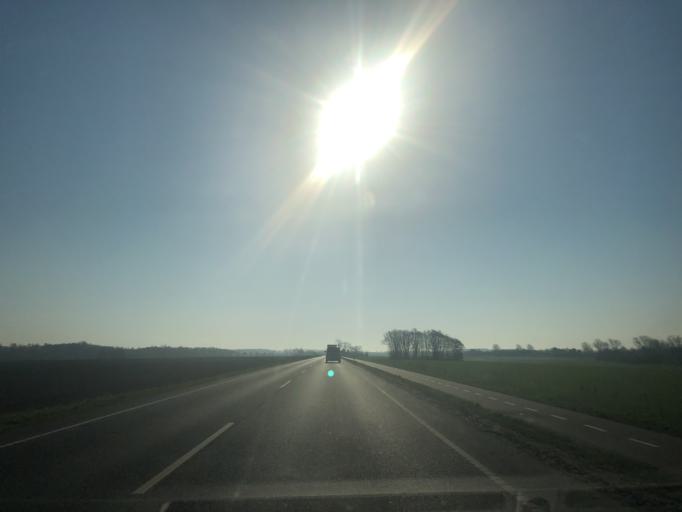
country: DK
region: Zealand
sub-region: Faxe Kommune
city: Ronnede
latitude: 55.2581
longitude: 12.0429
